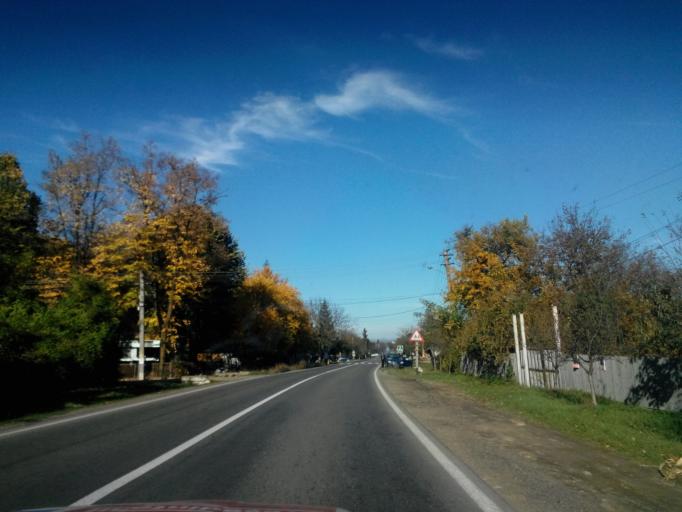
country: RO
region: Bacau
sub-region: Comuna Stefan Cel Mare
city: Stefan Cel Mare
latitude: 46.1999
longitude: 26.8877
